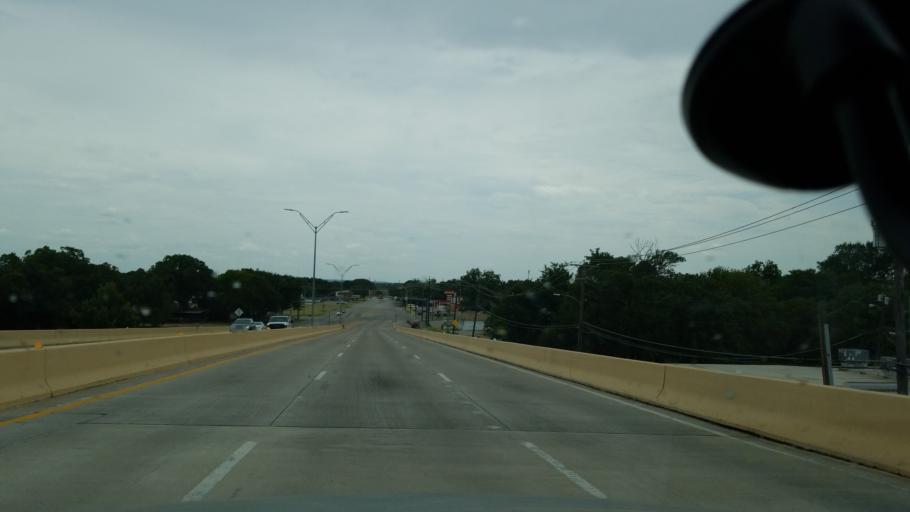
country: US
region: Texas
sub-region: Dallas County
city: Grand Prairie
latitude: 32.7445
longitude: -96.9946
